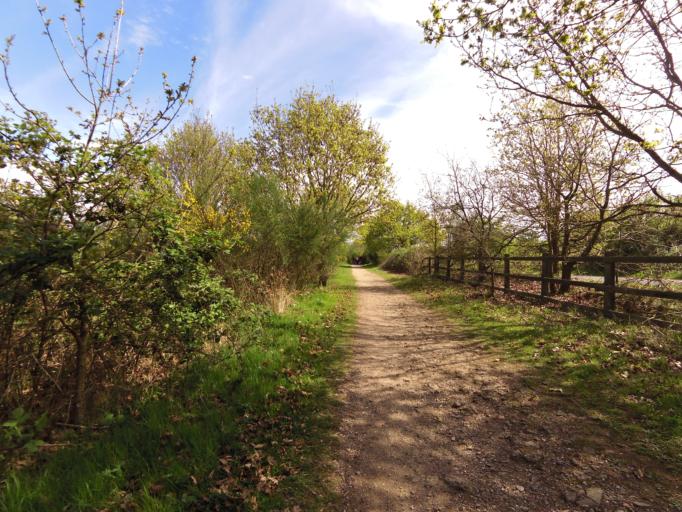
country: GB
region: England
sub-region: Essex
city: Mistley
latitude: 51.9859
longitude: 1.1086
